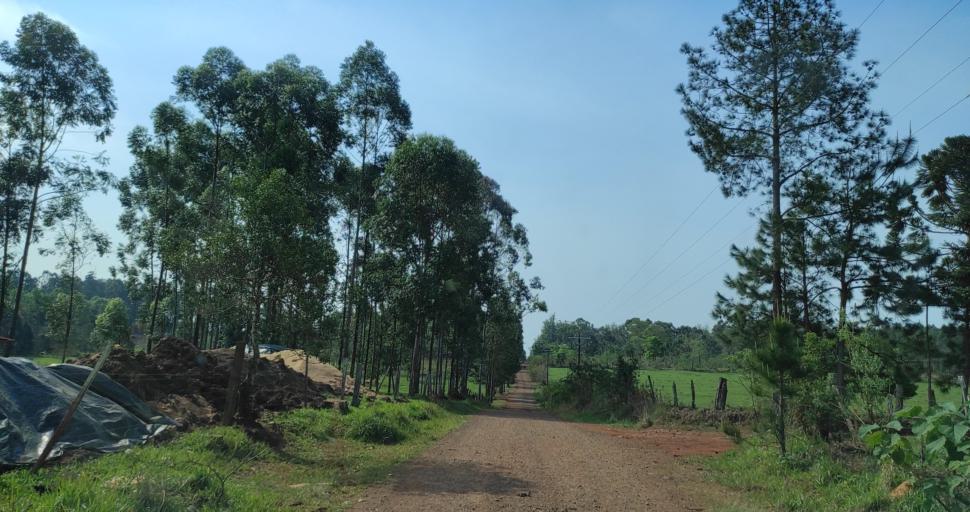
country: AR
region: Misiones
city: Capiovi
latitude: -26.8881
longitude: -55.0487
